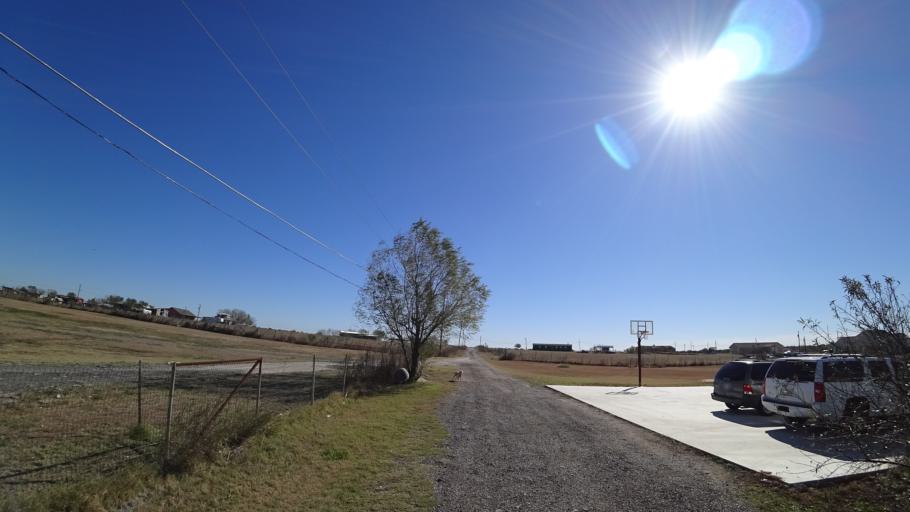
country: US
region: Texas
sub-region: Travis County
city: Garfield
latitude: 30.0995
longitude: -97.6197
